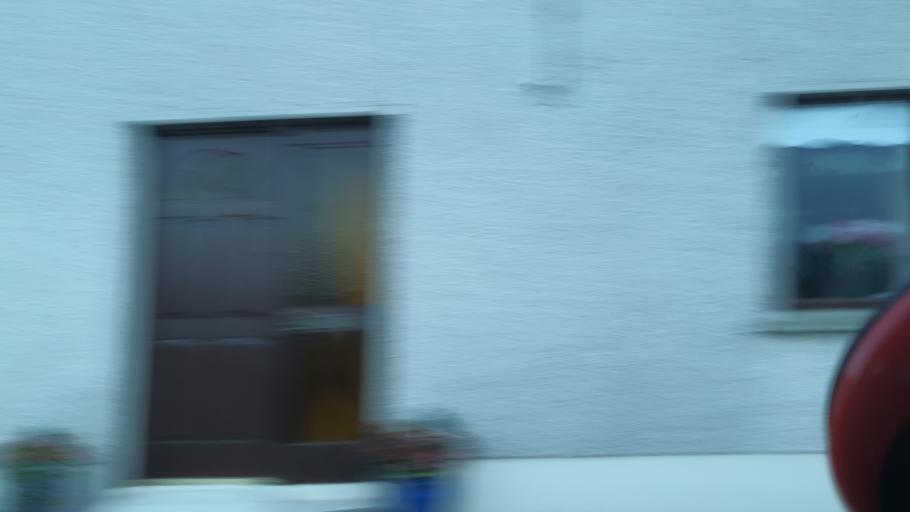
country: GB
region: Northern Ireland
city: Kilkeel
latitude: 54.0397
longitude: -6.0834
